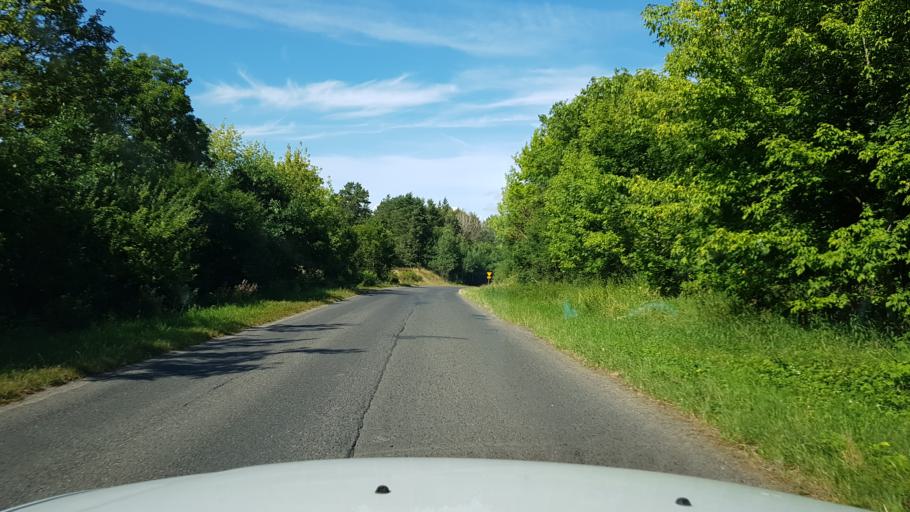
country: PL
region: West Pomeranian Voivodeship
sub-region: Powiat gryfinski
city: Stare Czarnowo
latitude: 53.2941
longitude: 14.7865
